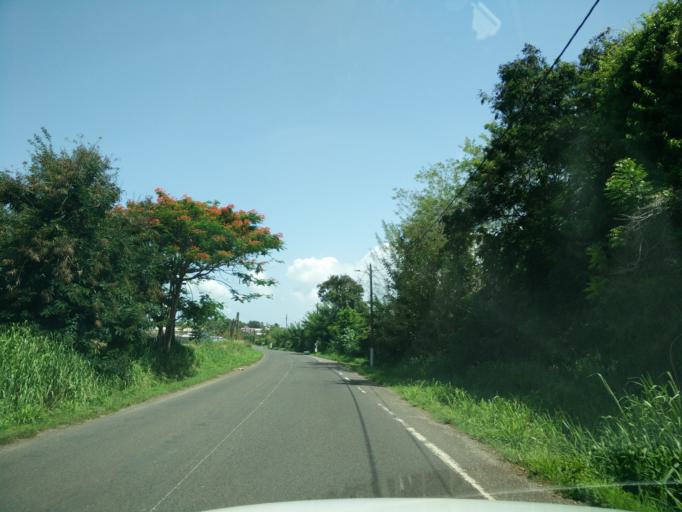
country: GP
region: Guadeloupe
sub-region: Guadeloupe
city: Petit-Bourg
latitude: 16.1762
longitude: -61.5868
